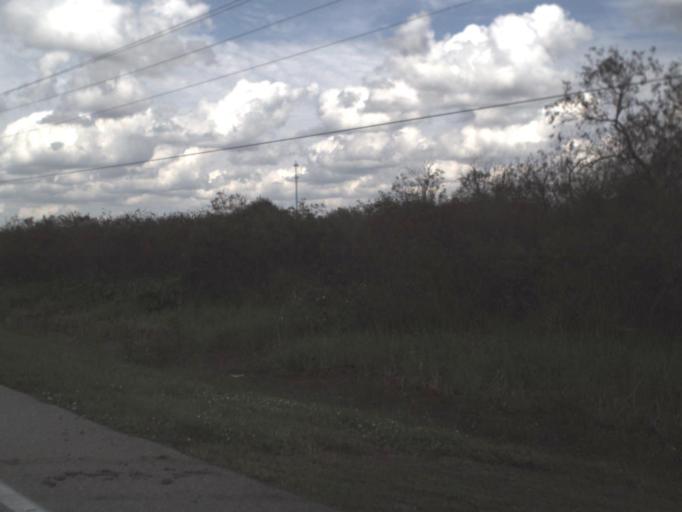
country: US
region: Florida
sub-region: Collier County
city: Immokalee
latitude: 26.5166
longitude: -81.4351
